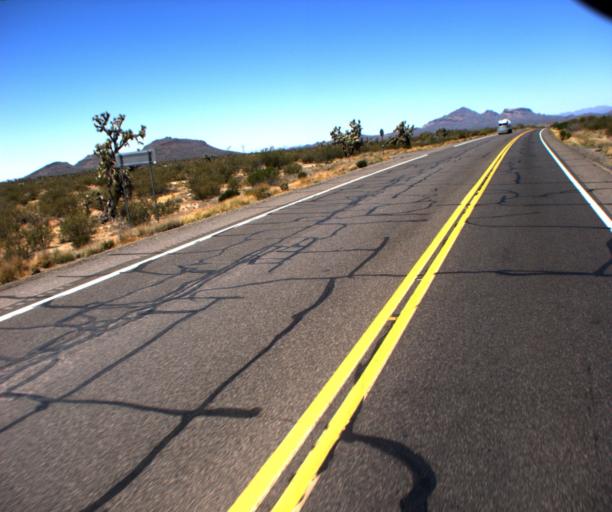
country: US
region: Arizona
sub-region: Yavapai County
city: Congress
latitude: 34.1856
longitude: -113.0454
